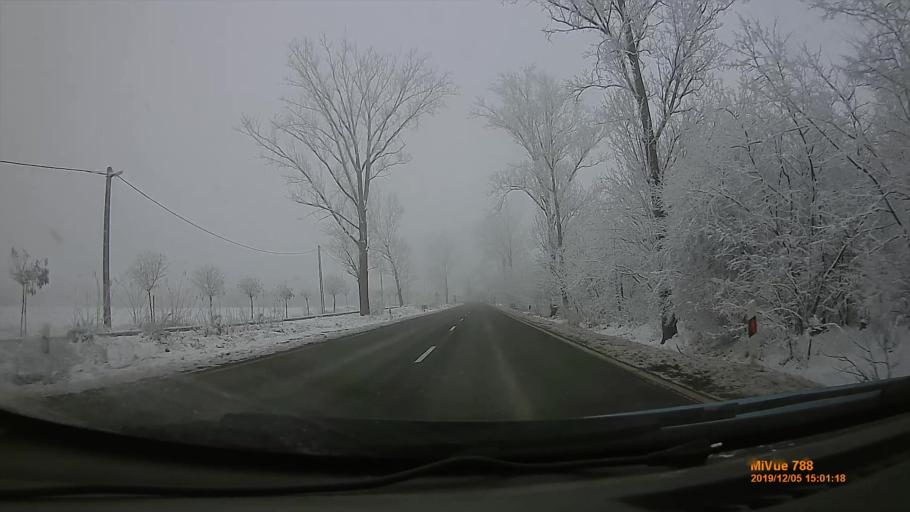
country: HU
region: Szabolcs-Szatmar-Bereg
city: Tiszanagyfalu
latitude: 48.0677
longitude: 21.5294
